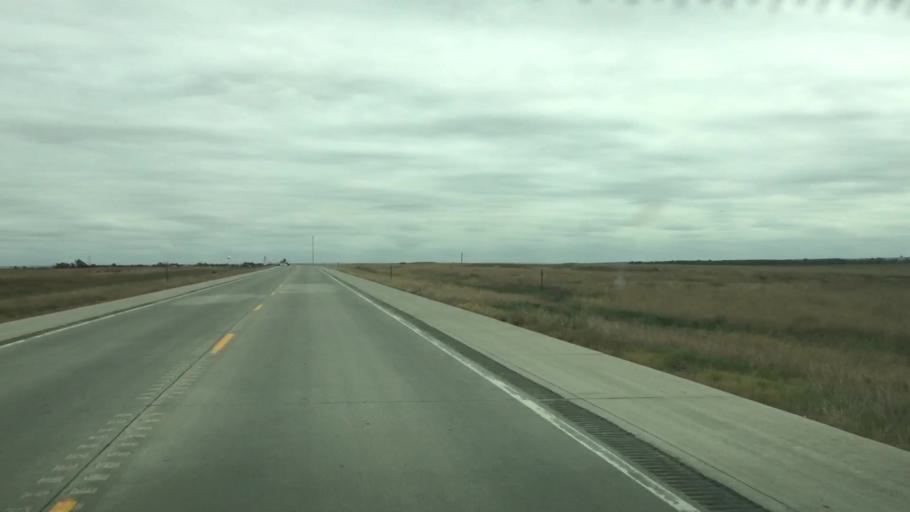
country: US
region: Colorado
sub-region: Kiowa County
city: Eads
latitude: 38.7644
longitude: -102.8284
